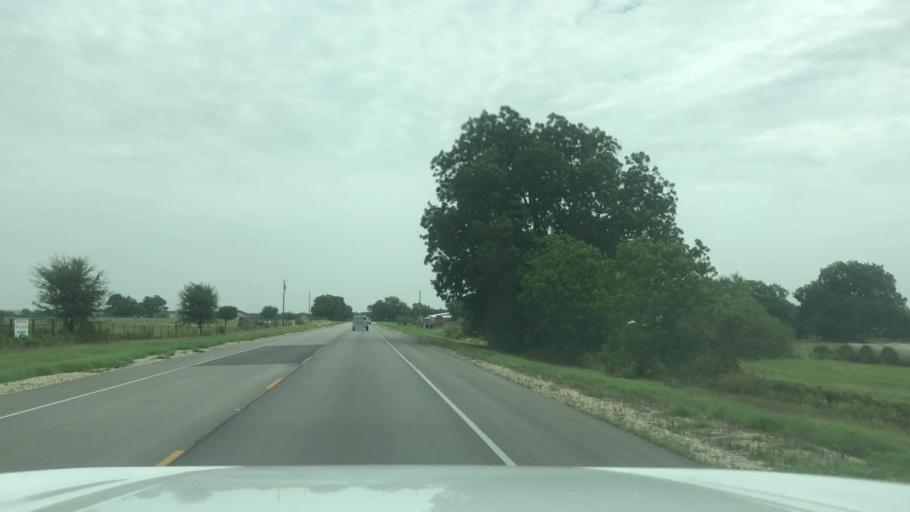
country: US
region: Texas
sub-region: Erath County
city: Dublin
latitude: 32.0904
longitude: -98.2817
